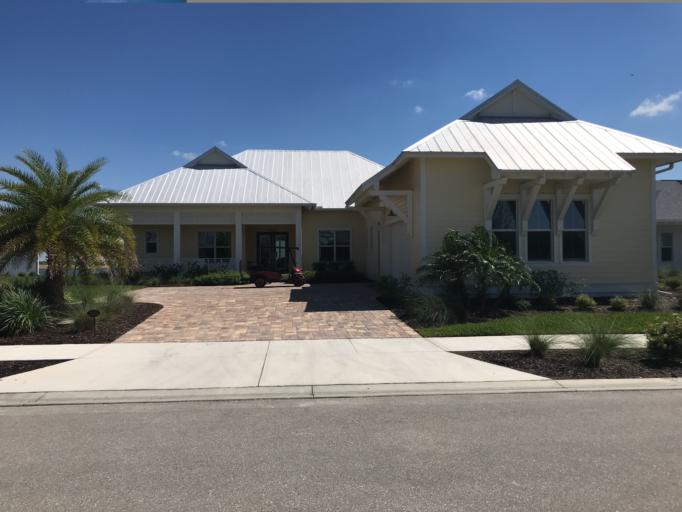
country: US
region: Florida
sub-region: Lee County
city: Fort Myers Shores
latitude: 26.7809
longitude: -81.7523
